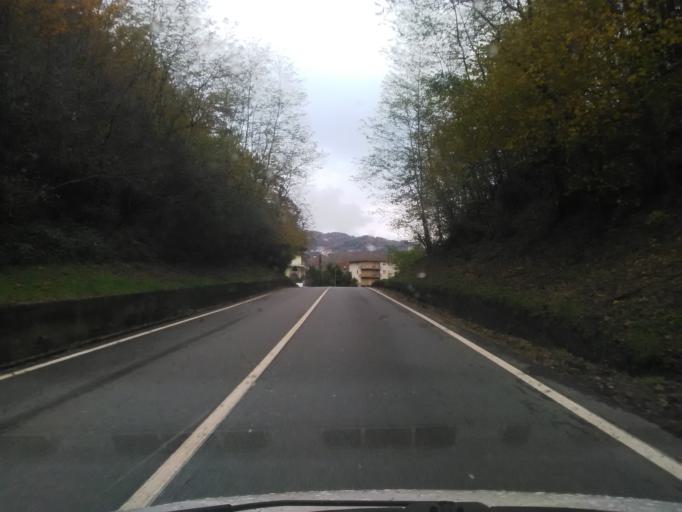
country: IT
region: Piedmont
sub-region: Provincia di Vercelli
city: Borgosesia
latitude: 45.7180
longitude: 8.3011
